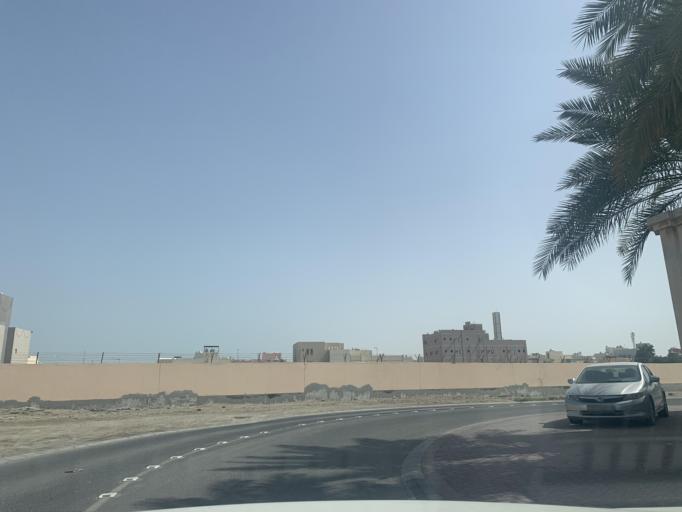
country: BH
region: Northern
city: Sitrah
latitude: 26.1665
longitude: 50.6277
